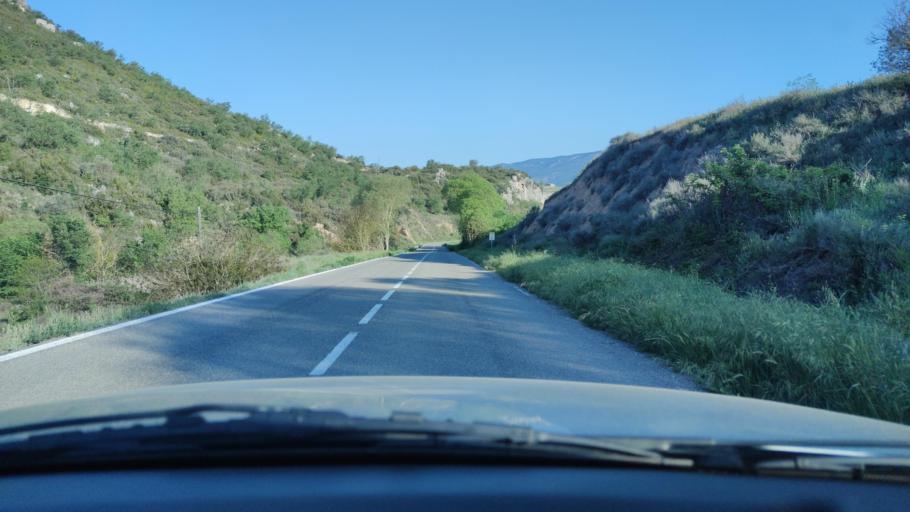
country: ES
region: Catalonia
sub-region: Provincia de Lleida
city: Artesa de Segre
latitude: 41.8835
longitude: 1.0001
